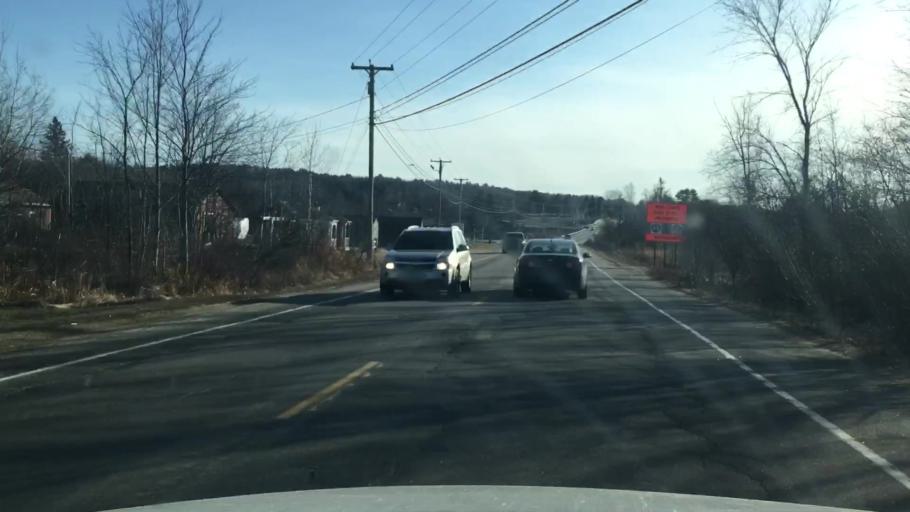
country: US
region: Maine
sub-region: Androscoggin County
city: Sabattus
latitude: 44.1057
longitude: -70.0879
